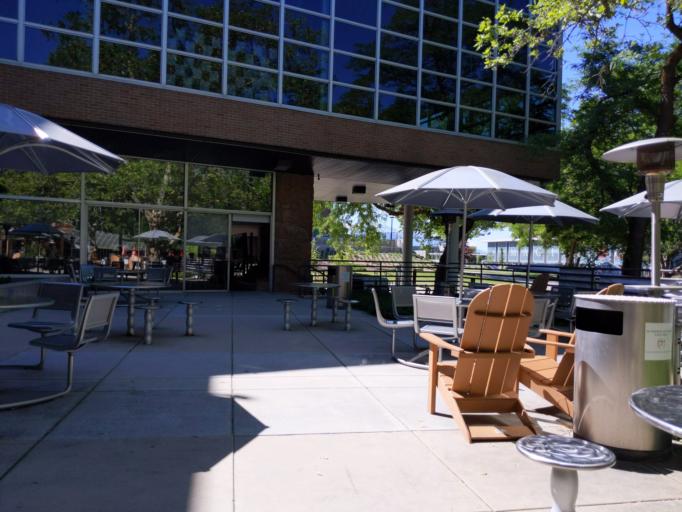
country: US
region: Utah
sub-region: Salt Lake County
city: Salt Lake City
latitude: 40.7646
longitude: -111.8457
